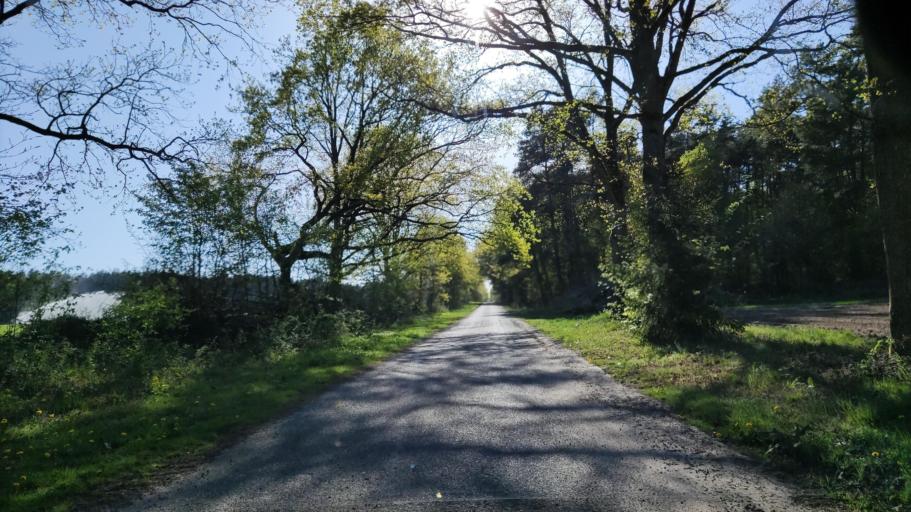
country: DE
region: Lower Saxony
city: Soderstorf
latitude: 53.1606
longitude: 10.1399
